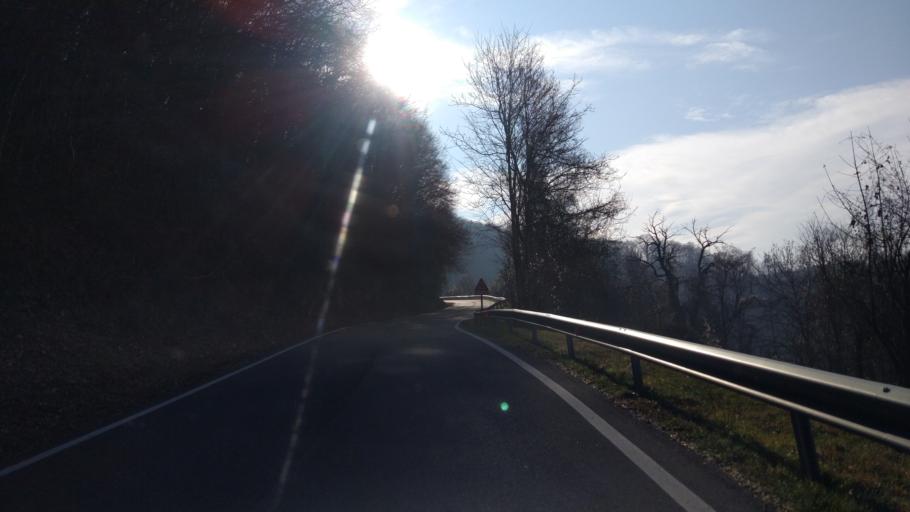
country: IT
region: Veneto
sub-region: Provincia di Verona
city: Selva di Progno
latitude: 45.6071
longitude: 11.1685
